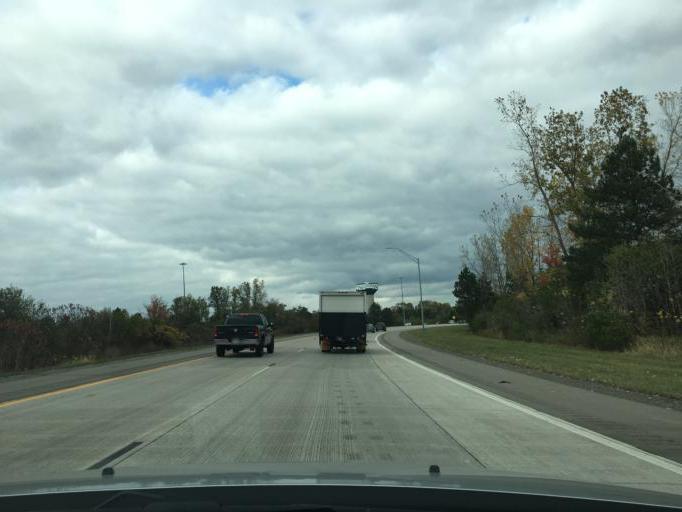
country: US
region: Michigan
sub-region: Oakland County
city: Farmington Hills
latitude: 42.4861
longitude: -83.4261
